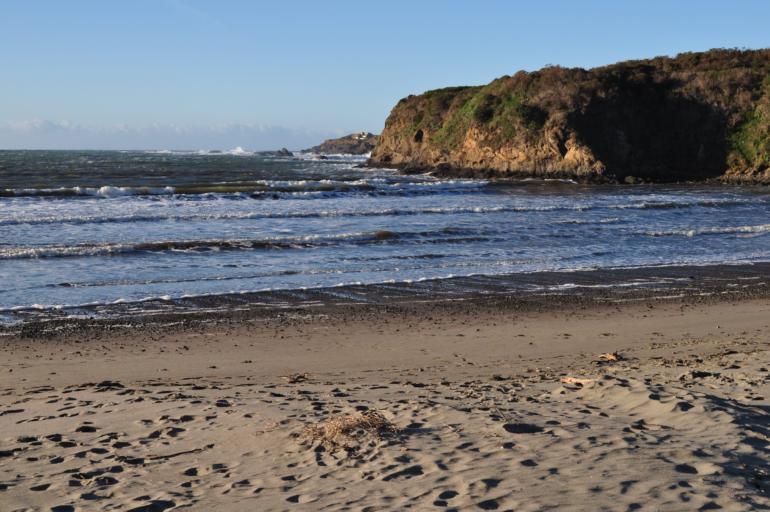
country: US
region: California
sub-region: Mendocino County
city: Fort Bragg
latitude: 39.3608
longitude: -123.8167
